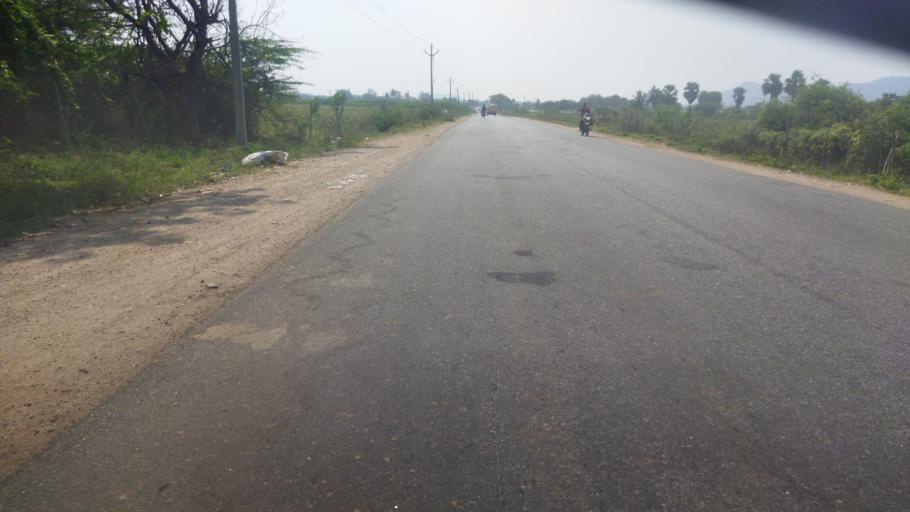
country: IN
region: Telangana
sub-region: Nalgonda
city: Nalgonda
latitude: 17.0892
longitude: 79.2851
